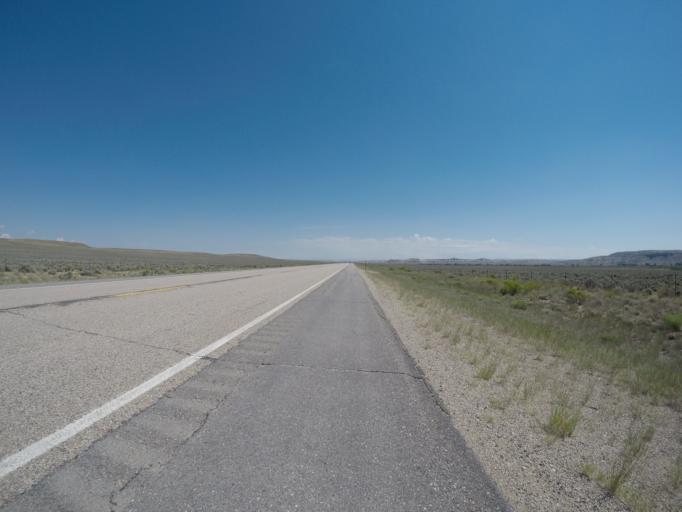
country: US
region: Wyoming
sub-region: Sublette County
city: Marbleton
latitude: 42.4343
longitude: -110.1032
